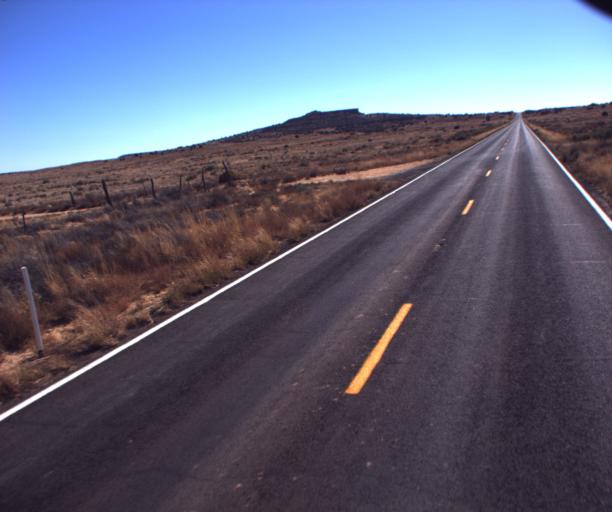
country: US
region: Arizona
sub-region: Navajo County
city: First Mesa
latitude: 35.9702
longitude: -110.6944
